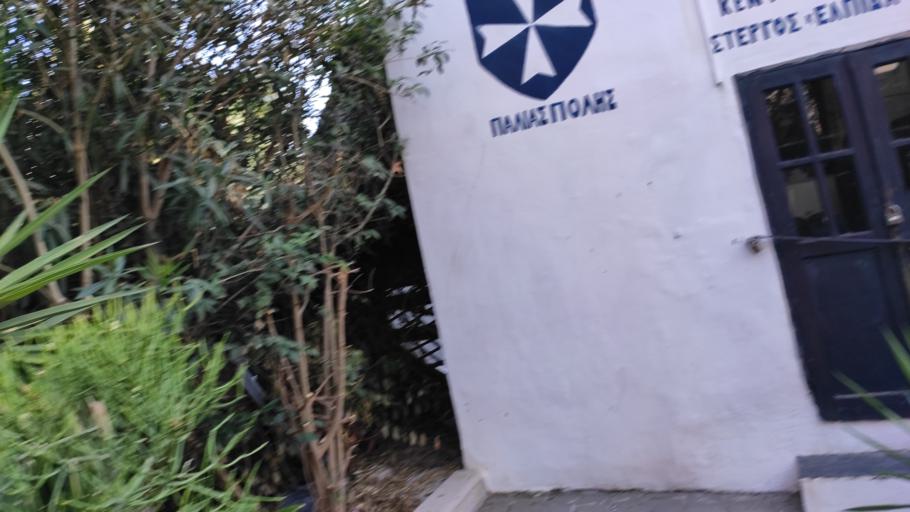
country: GR
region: South Aegean
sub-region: Nomos Dodekanisou
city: Rodos
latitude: 36.4421
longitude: 28.2318
